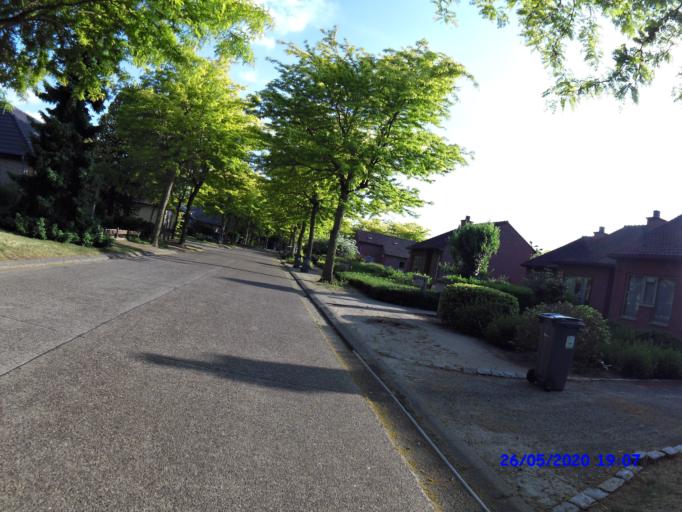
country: BE
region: Flanders
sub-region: Provincie Antwerpen
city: Olen
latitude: 51.1443
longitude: 4.8372
